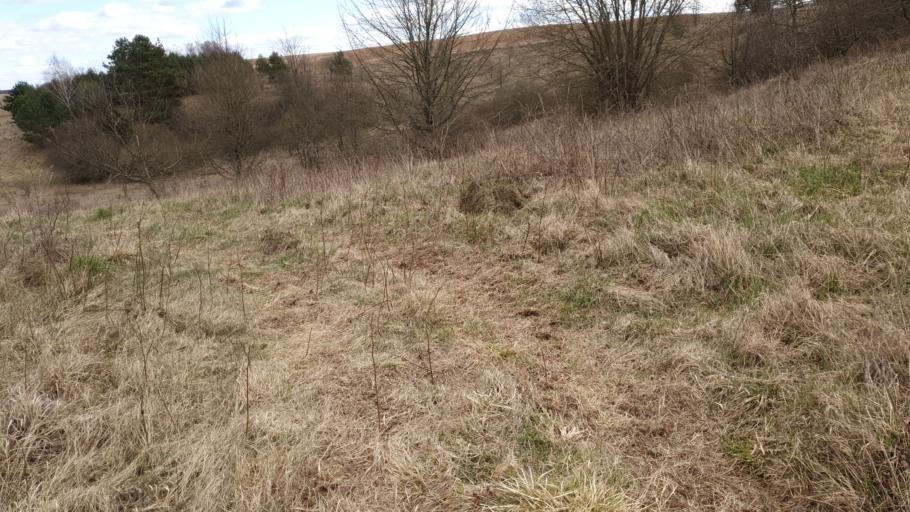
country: LT
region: Vilnius County
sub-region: Vilniaus Rajonas
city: Vievis
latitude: 54.6430
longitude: 24.7306
